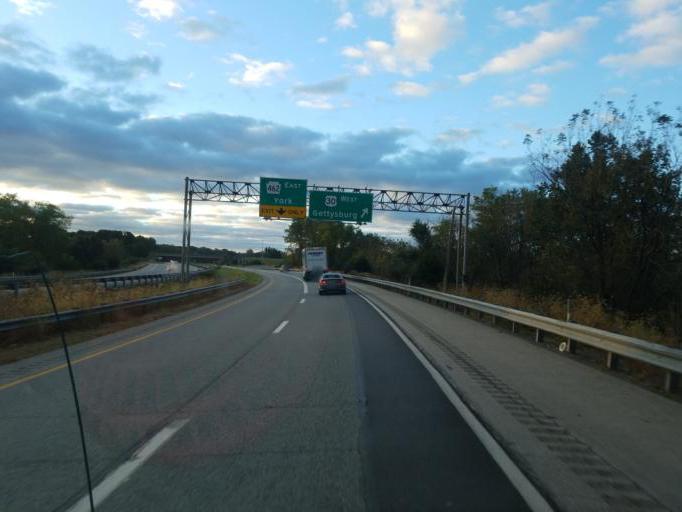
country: US
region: Pennsylvania
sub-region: York County
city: Shiloh
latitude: 39.9408
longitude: -76.8011
